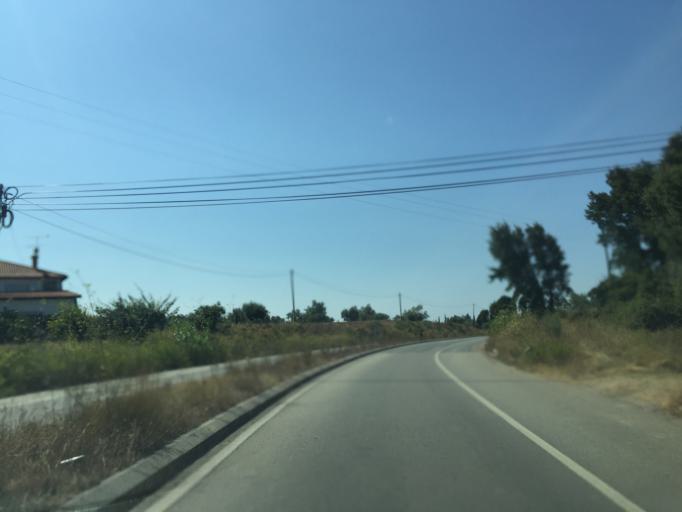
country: PT
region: Aveiro
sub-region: Mealhada
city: Mealhada
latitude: 40.3668
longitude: -8.4570
